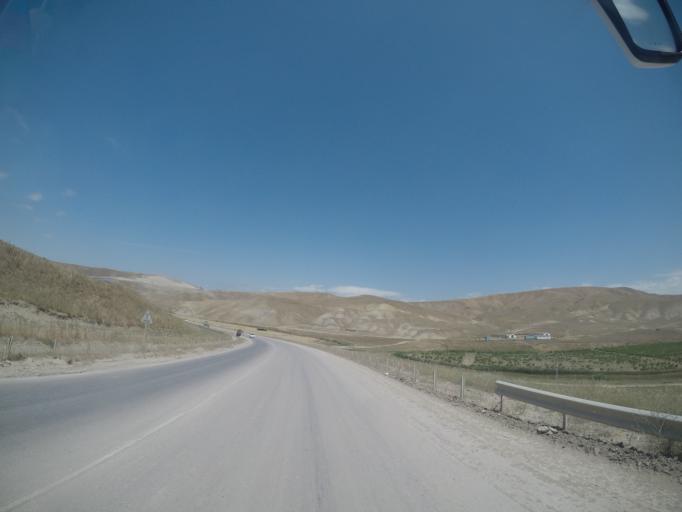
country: AZ
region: Samaxi
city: Shamakhi
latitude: 40.5540
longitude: 48.7643
